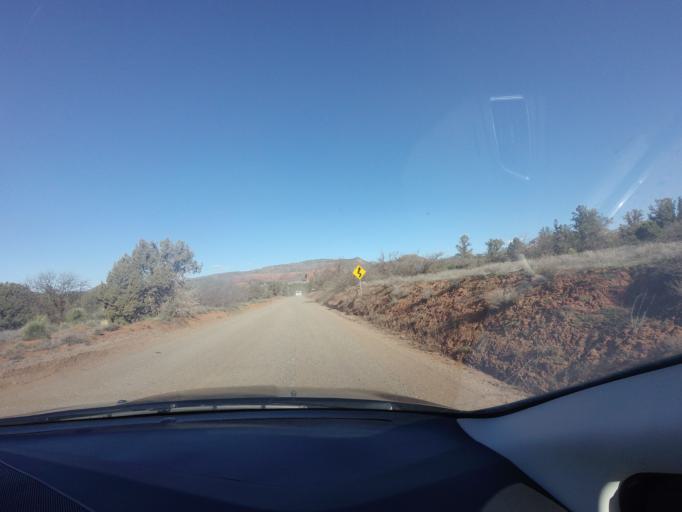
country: US
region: Arizona
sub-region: Yavapai County
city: West Sedona
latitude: 34.8121
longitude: -111.8084
